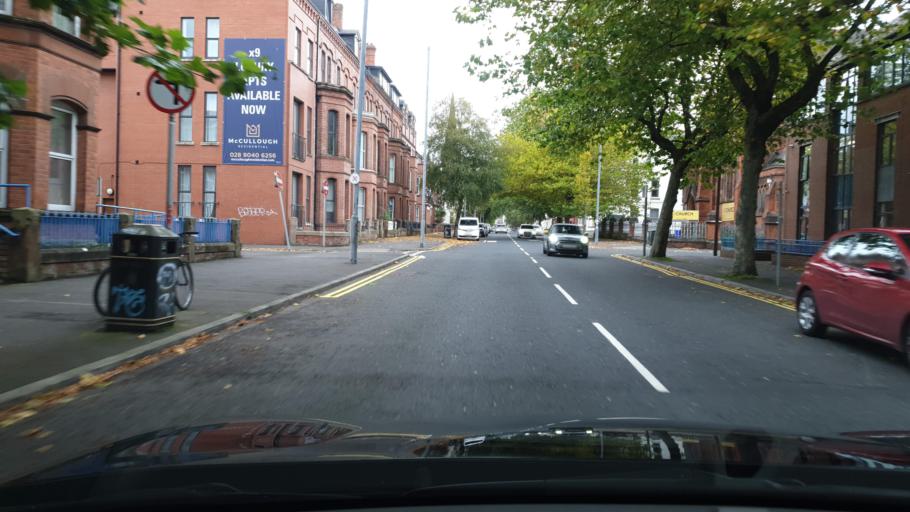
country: GB
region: Northern Ireland
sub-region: City of Belfast
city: Belfast
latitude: 54.5862
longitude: -5.9268
